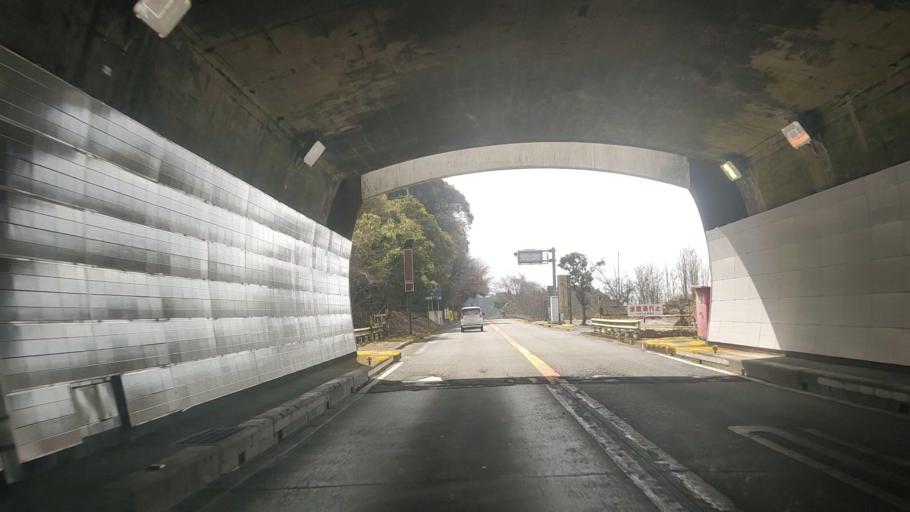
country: JP
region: Kumamoto
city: Hitoyoshi
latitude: 32.0890
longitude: 130.8017
